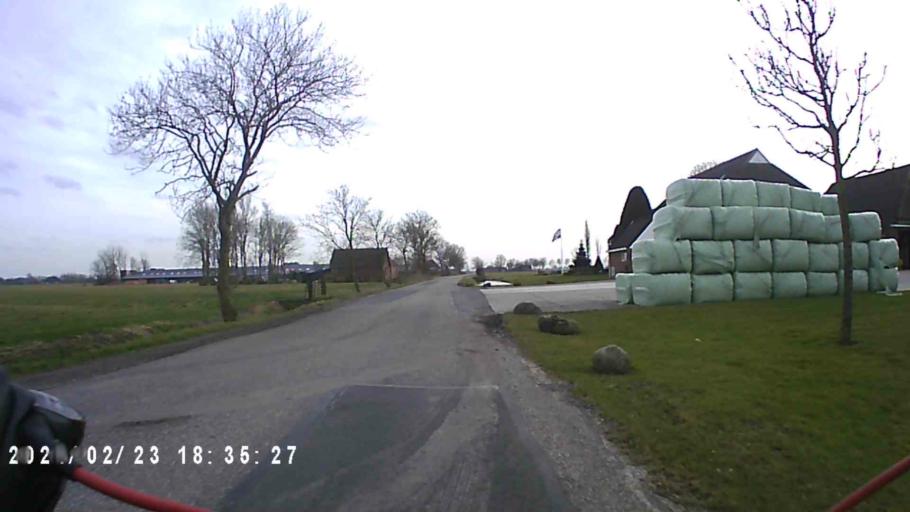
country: NL
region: Groningen
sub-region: Gemeente Bedum
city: Bedum
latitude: 53.3423
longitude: 6.6044
